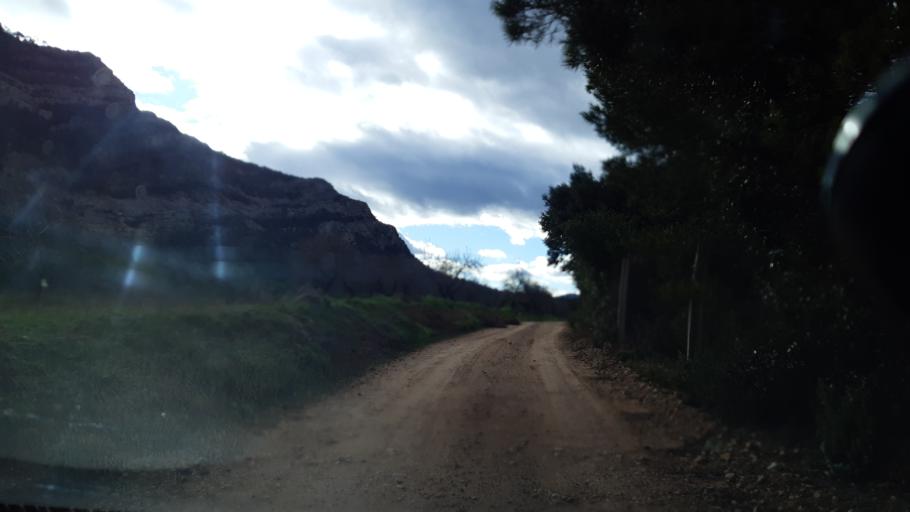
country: ES
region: Aragon
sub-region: Provincia de Teruel
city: Valderrobres
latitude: 40.8538
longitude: 0.2279
